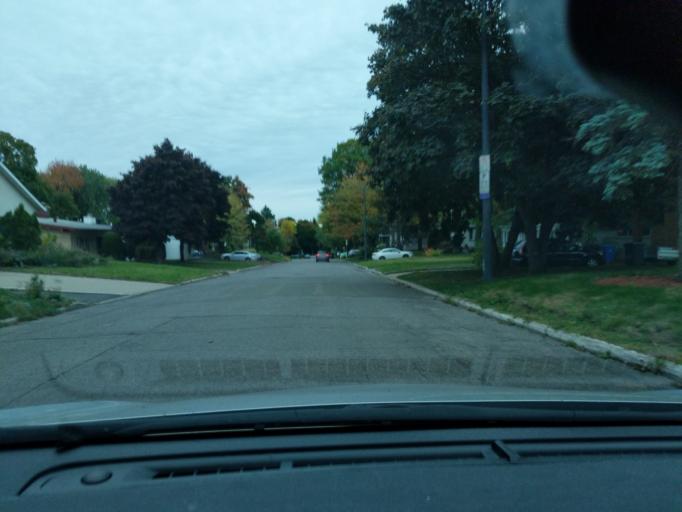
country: CA
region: Quebec
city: L'Ancienne-Lorette
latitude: 46.7669
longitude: -71.2784
